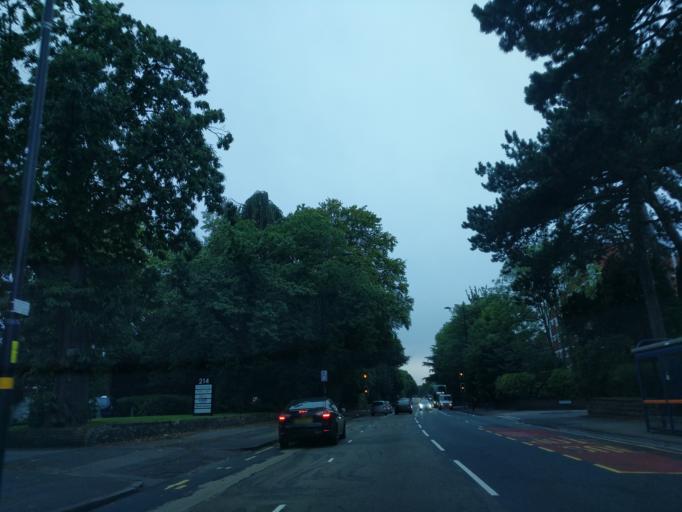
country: GB
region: England
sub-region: Sandwell
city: Smethwick
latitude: 52.4718
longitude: -1.9474
